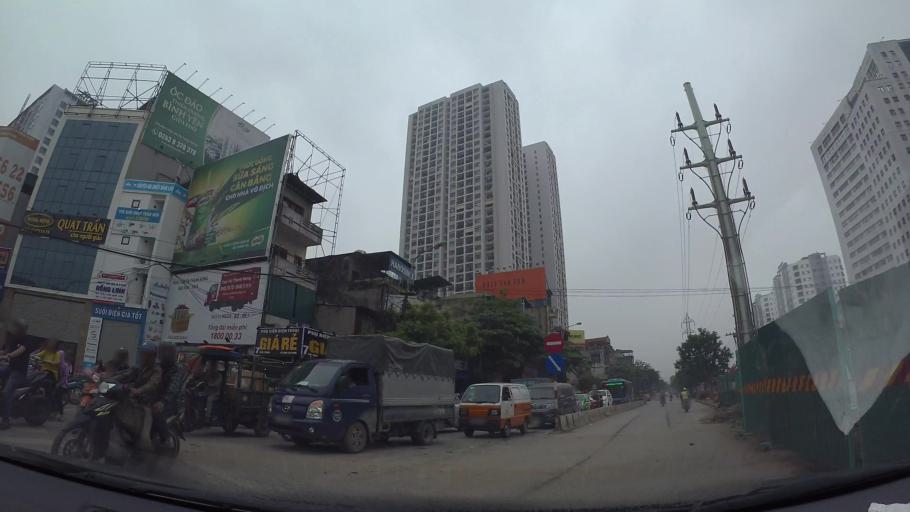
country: VN
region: Ha Noi
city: Hai BaTrung
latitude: 20.9962
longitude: 105.8625
